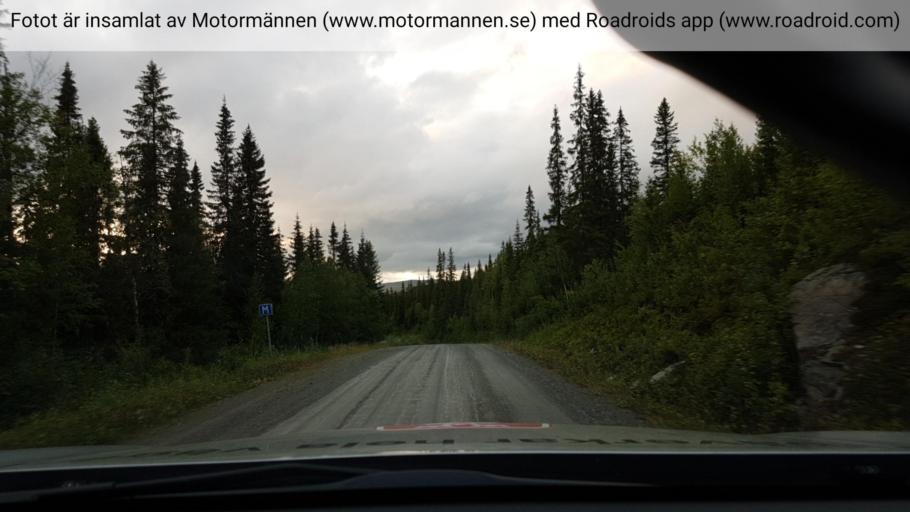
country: SE
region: Vaesterbotten
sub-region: Vilhelmina Kommun
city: Sjoberg
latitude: 65.5004
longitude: 15.4837
